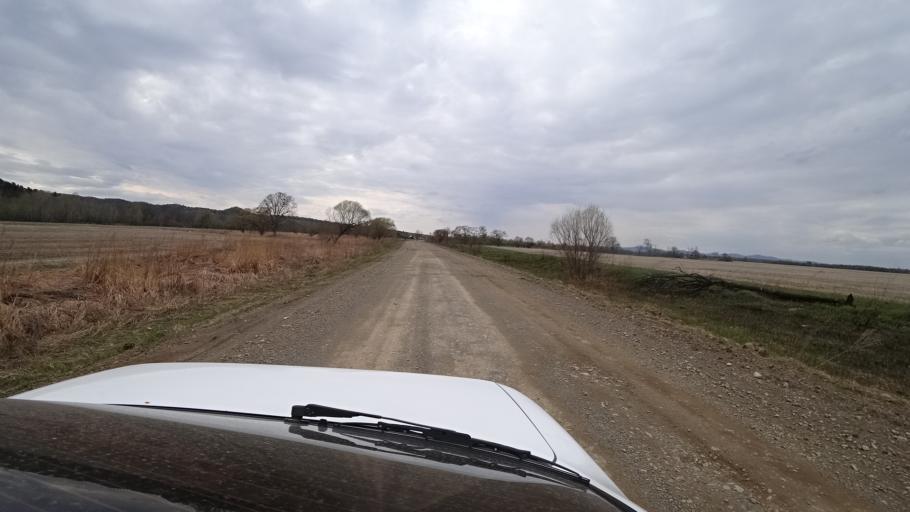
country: RU
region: Primorskiy
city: Novopokrovka
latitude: 45.4894
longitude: 134.4611
